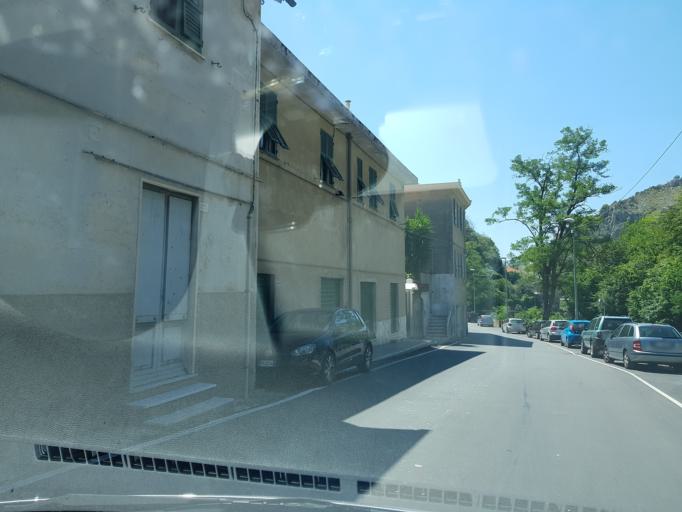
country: IT
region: Liguria
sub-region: Provincia di Genova
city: San Teodoro
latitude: 44.4407
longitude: 8.8552
